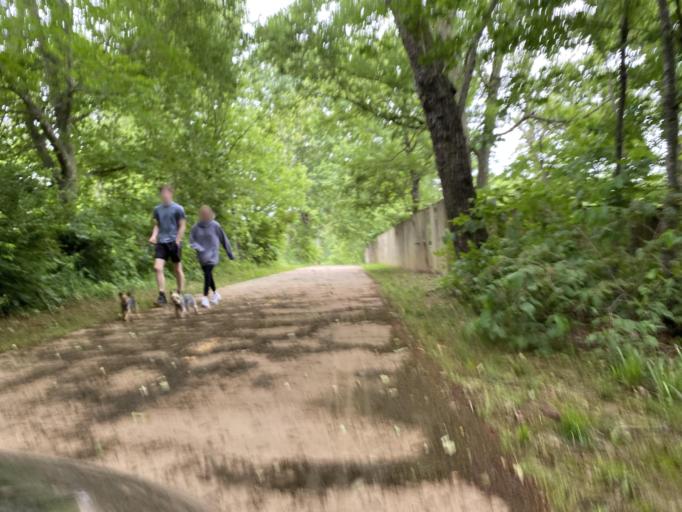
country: US
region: Arkansas
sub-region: Benton County
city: Bentonville
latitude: 36.3689
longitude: -94.2351
